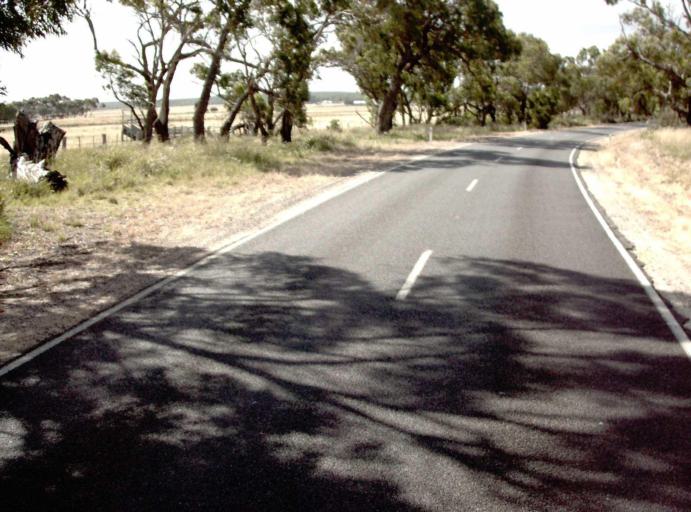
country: AU
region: Victoria
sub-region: Wellington
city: Sale
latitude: -38.2838
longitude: 147.1534
